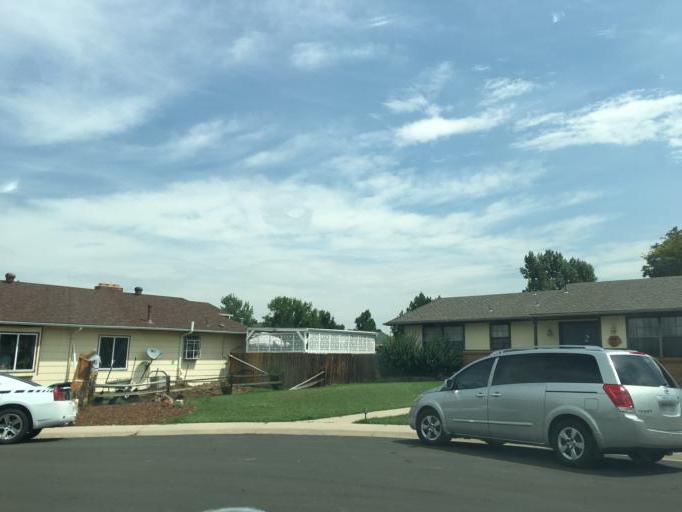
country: US
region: Colorado
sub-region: Adams County
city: Aurora
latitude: 39.7296
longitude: -104.8053
